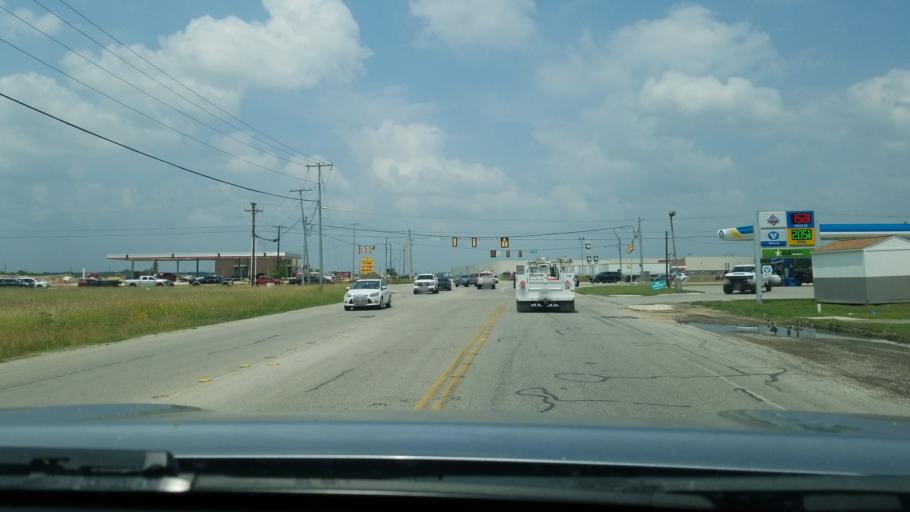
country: US
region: Texas
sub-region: Comal County
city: New Braunfels
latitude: 29.7403
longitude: -98.0941
